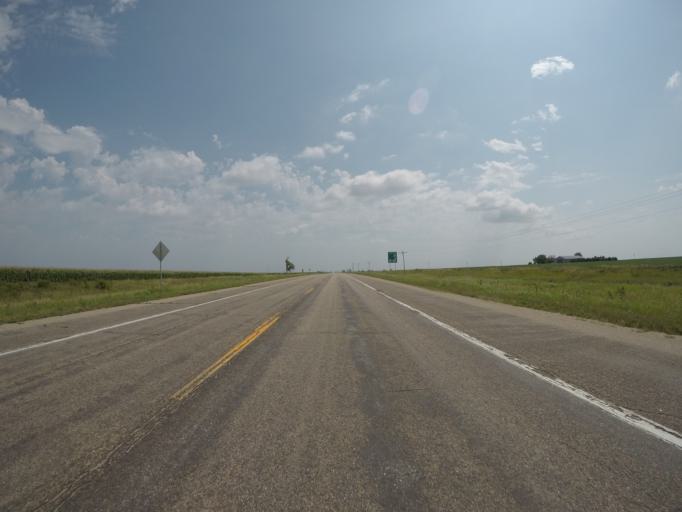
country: US
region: Nebraska
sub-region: Clay County
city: Clay Center
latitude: 40.4266
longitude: -98.0515
